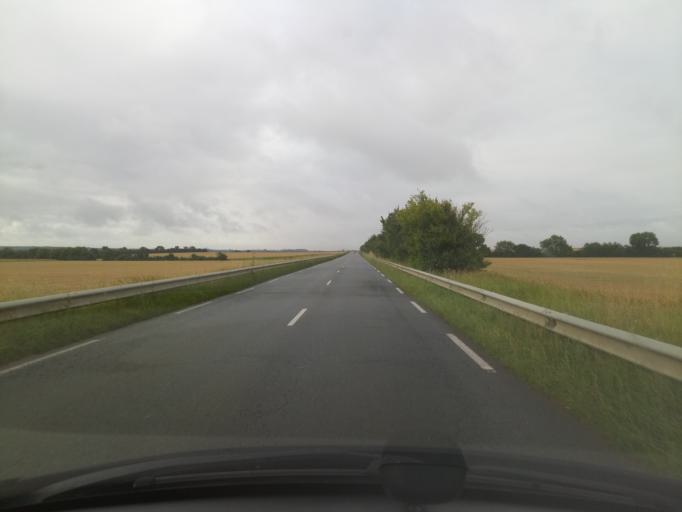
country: FR
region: Poitou-Charentes
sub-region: Departement de la Charente-Maritime
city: Saint-Jean-de-Liversay
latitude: 46.2075
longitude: -0.8744
